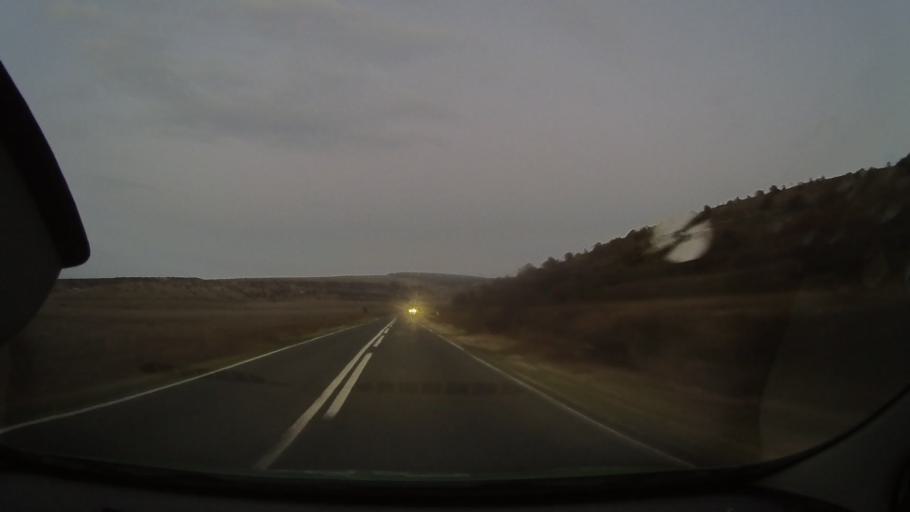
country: RO
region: Constanta
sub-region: Comuna Ion Corvin
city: Ion Corvin
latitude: 44.1090
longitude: 27.7572
